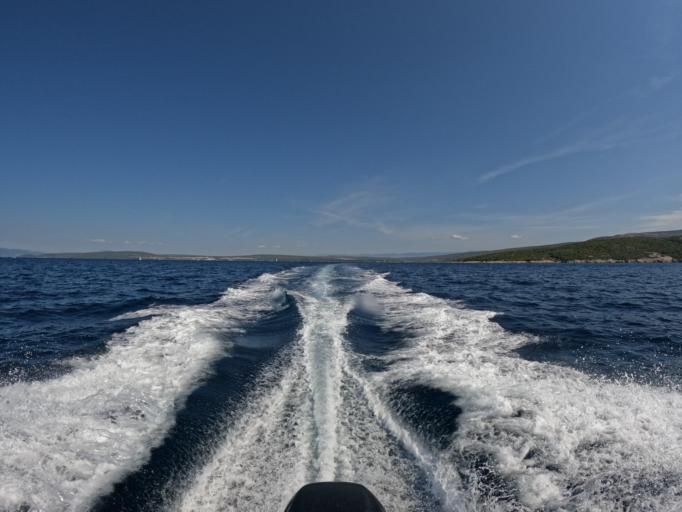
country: HR
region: Primorsko-Goranska
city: Punat
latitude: 44.9719
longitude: 14.6088
